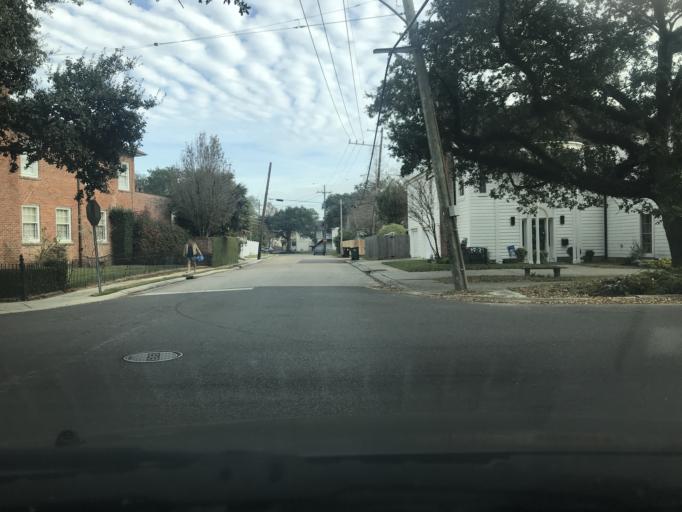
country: US
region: Louisiana
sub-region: Orleans Parish
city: New Orleans
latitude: 29.9546
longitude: -90.1078
